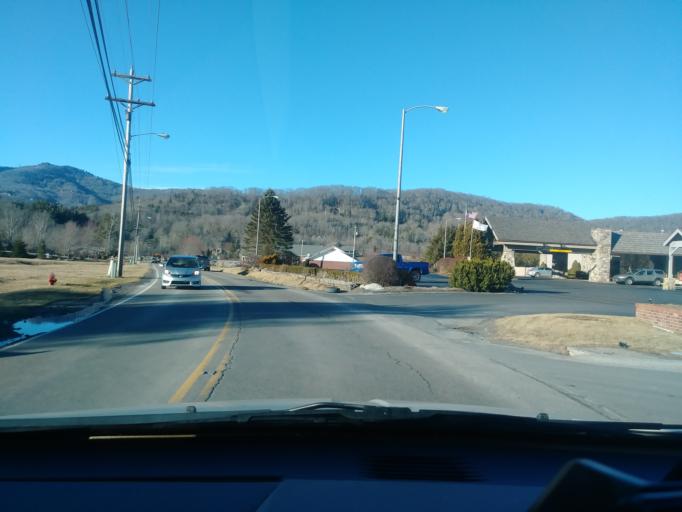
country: US
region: North Carolina
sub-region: Avery County
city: Banner Elk
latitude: 36.1488
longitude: -81.8605
